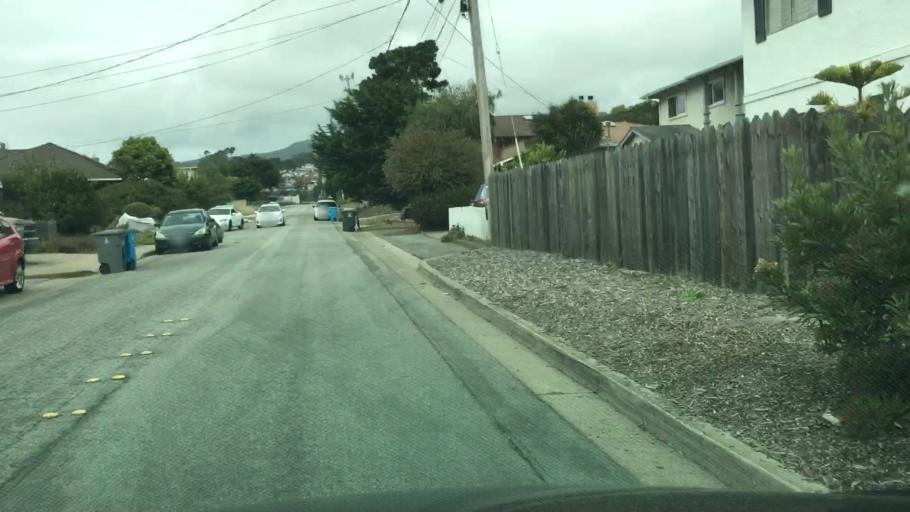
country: US
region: California
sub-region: San Mateo County
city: Moss Beach
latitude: 37.5236
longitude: -122.5150
